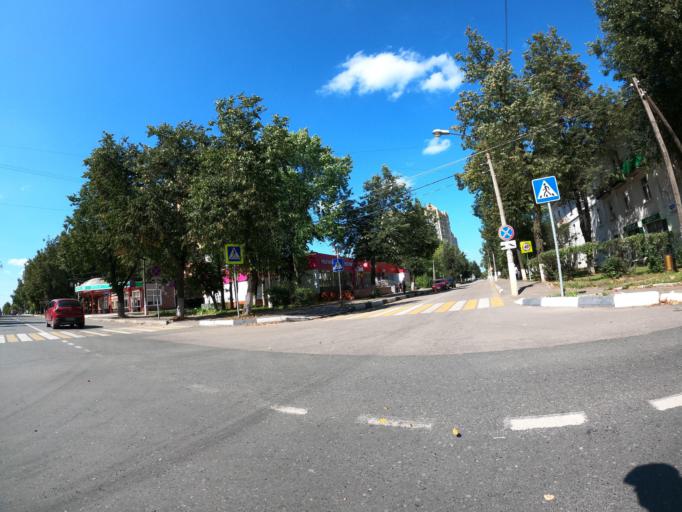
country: RU
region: Moskovskaya
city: Stupino
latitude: 54.8863
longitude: 38.0871
